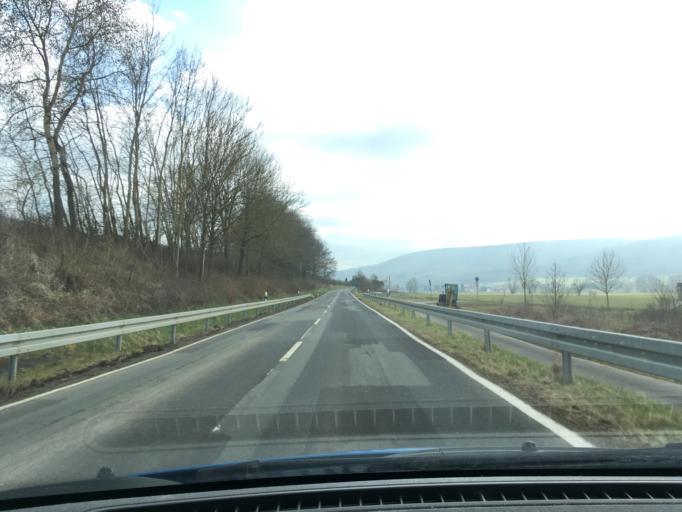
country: DE
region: Lower Saxony
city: Bodenfelde
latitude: 51.5798
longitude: 9.5947
